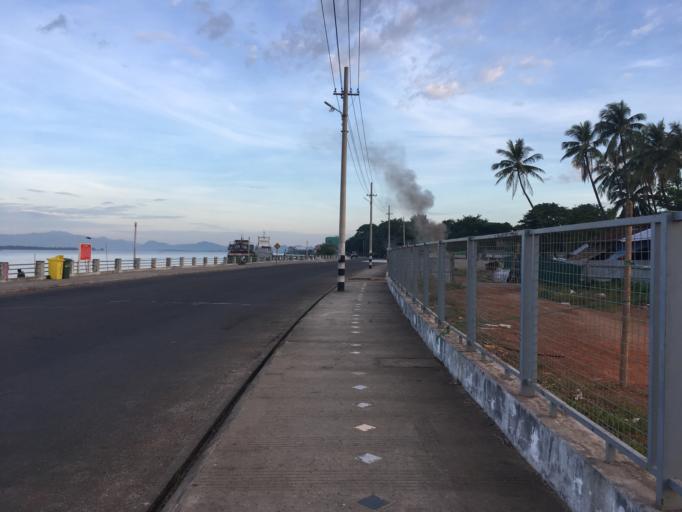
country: MM
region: Mon
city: Mawlamyine
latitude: 16.4630
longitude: 97.6226
